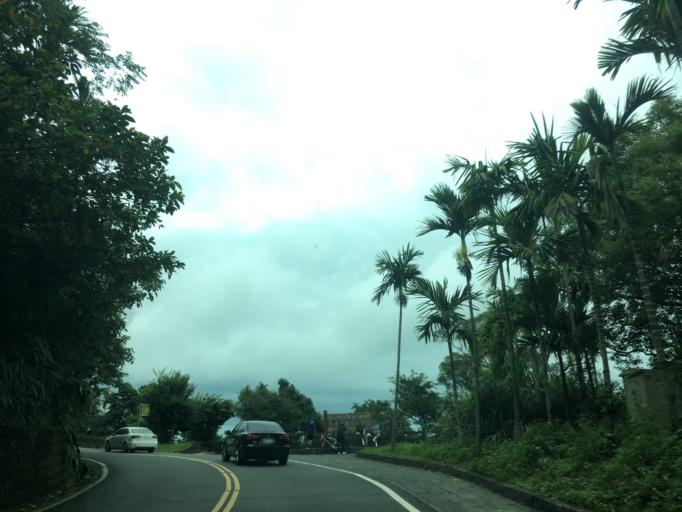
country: TW
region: Taiwan
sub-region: Yunlin
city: Douliu
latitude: 23.5643
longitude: 120.5921
